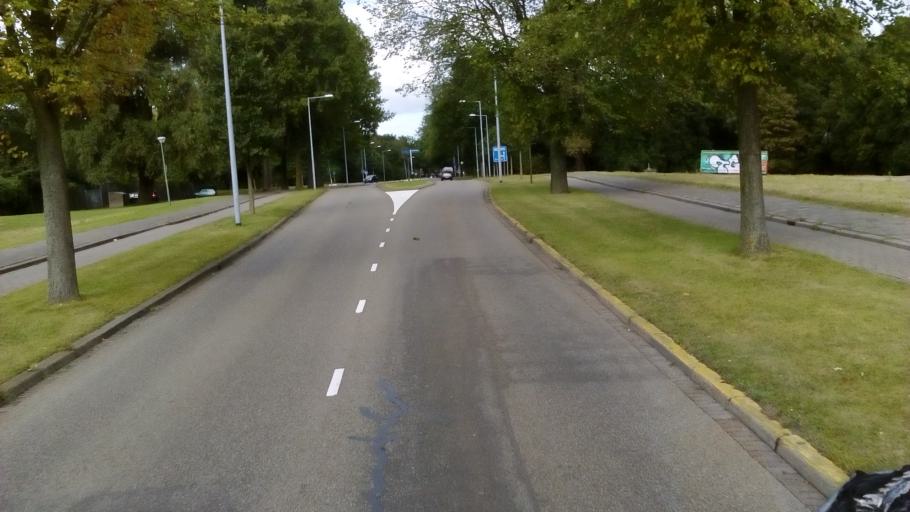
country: NL
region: South Holland
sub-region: Gemeente Schiedam
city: Schiedam
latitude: 51.9051
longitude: 4.3974
